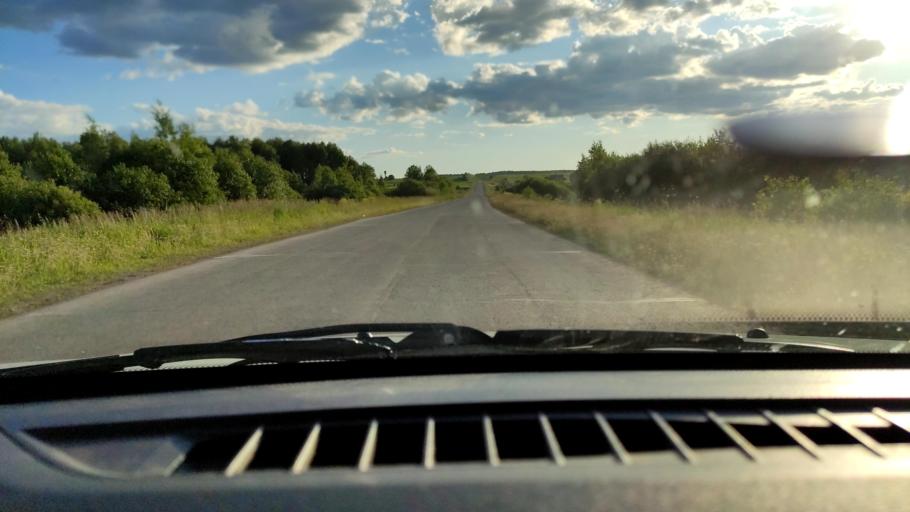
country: RU
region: Perm
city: Uinskoye
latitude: 57.0719
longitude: 56.5866
